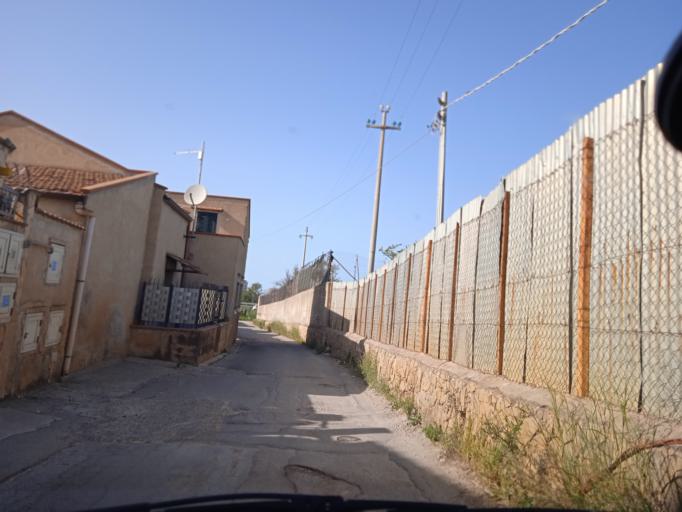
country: IT
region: Sicily
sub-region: Palermo
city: Portella di Mare
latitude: 38.0816
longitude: 13.4567
